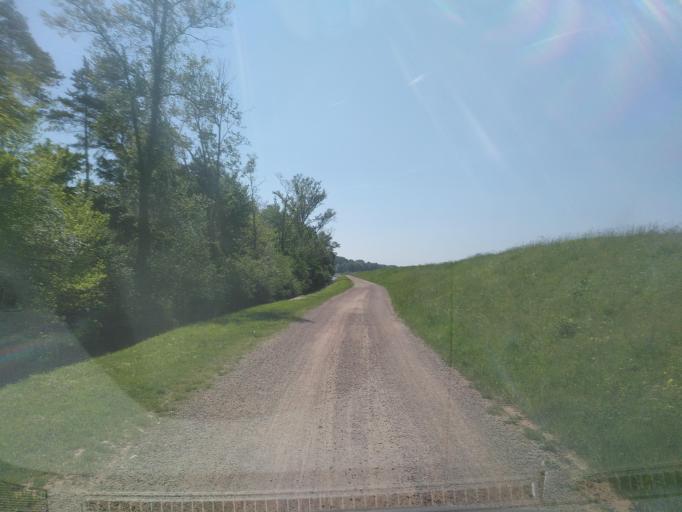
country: DE
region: Baden-Wuerttemberg
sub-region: Freiburg Region
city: Breisach am Rhein
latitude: 48.0635
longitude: 7.5743
